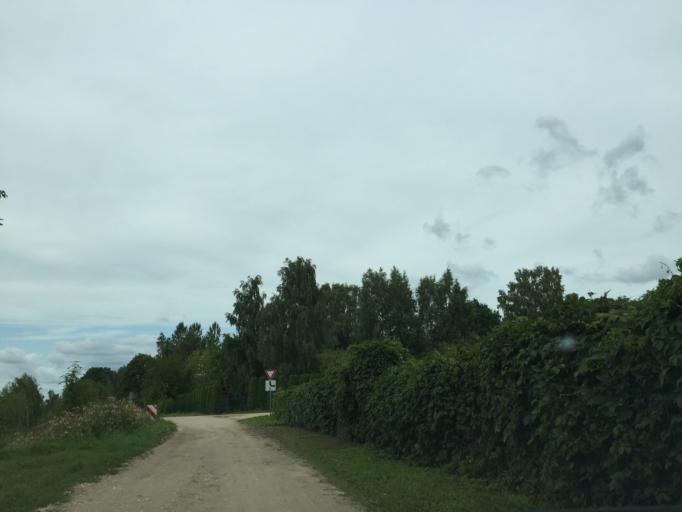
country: LV
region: Kegums
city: Kegums
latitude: 56.7461
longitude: 24.7082
